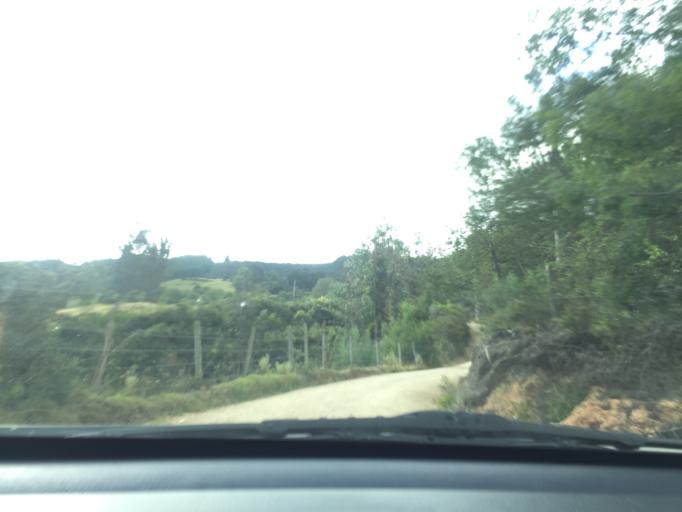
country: CO
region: Cundinamarca
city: Tocancipa
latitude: 4.9285
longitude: -73.8947
